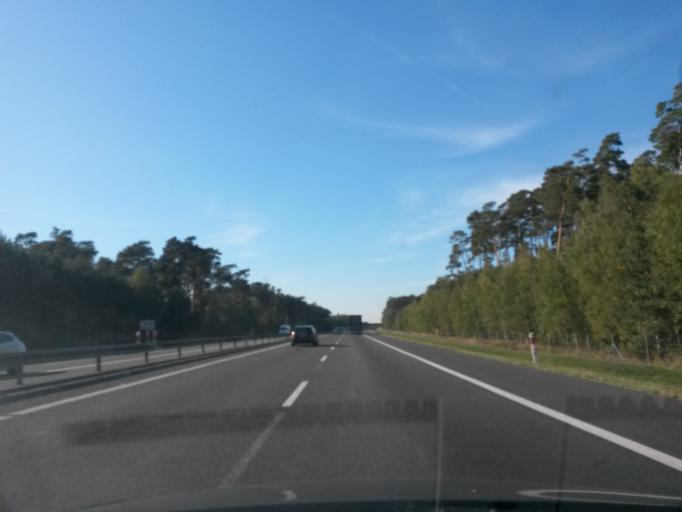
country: PL
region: Opole Voivodeship
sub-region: Powiat opolski
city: Niemodlin
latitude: 50.6680
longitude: 17.6760
